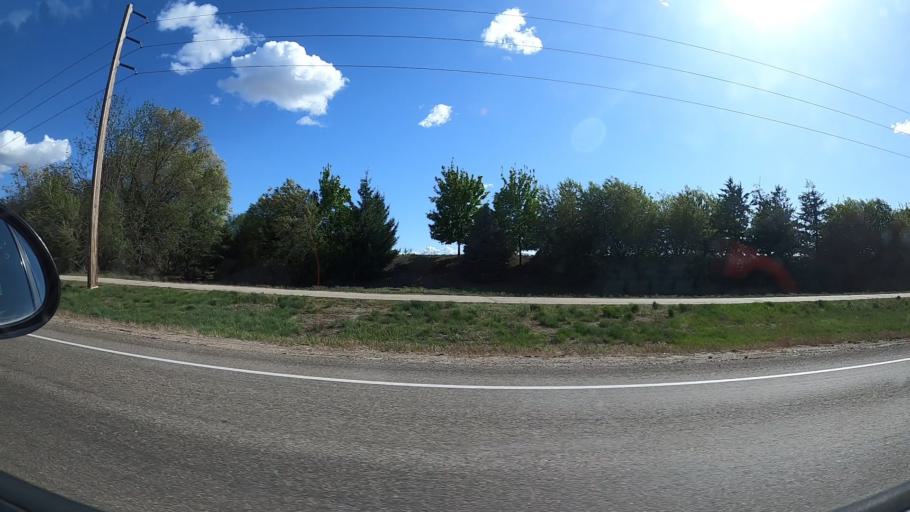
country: US
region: Idaho
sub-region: Ada County
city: Eagle
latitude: 43.6949
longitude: -116.3781
